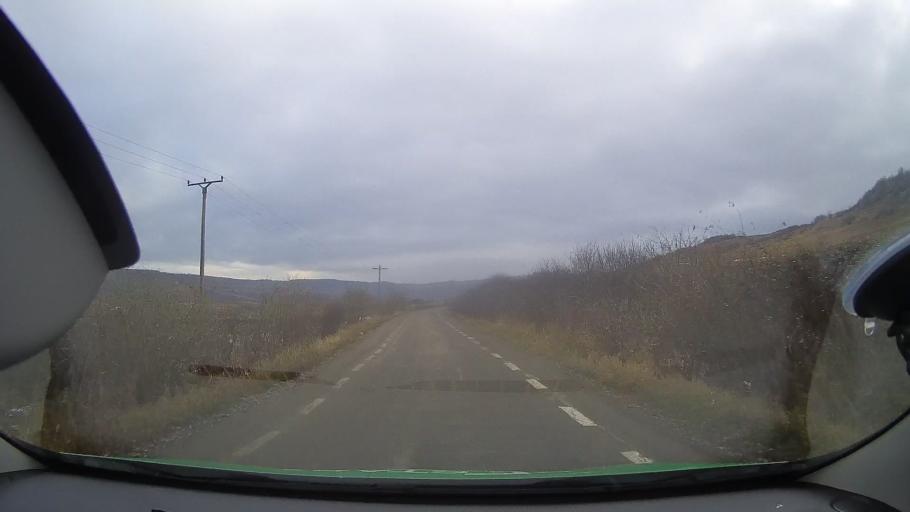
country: RO
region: Mures
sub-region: Comuna Atintis
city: Atintis
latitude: 46.4082
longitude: 24.0854
